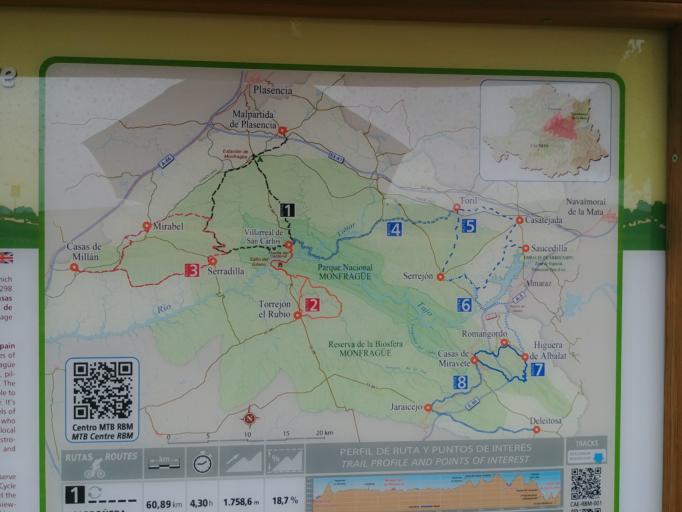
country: ES
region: Extremadura
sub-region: Provincia de Caceres
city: Torrejon el Rubio
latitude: 39.8478
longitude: -6.0294
